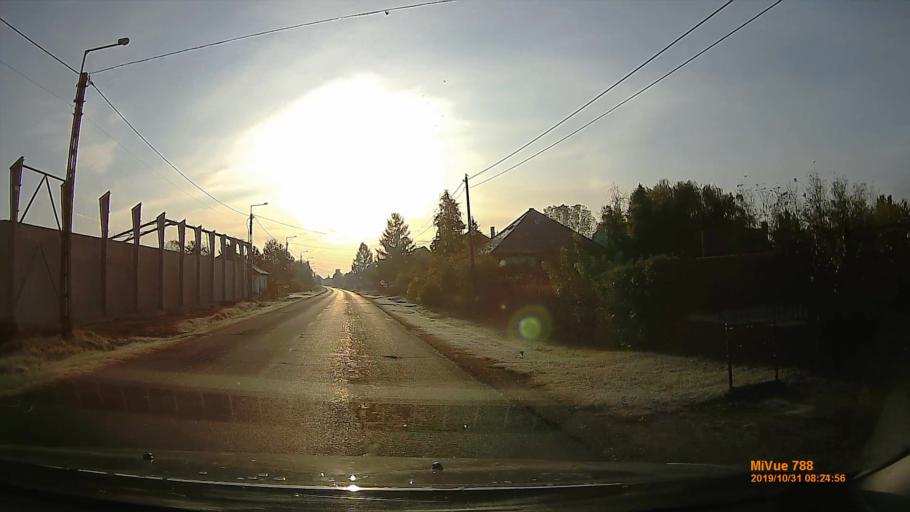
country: HU
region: Pest
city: Tapiobicske
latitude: 47.3679
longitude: 19.6641
